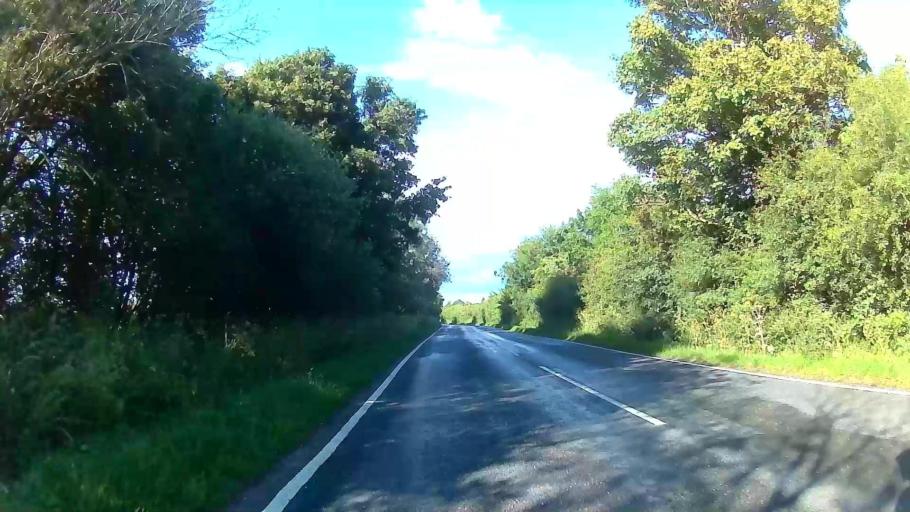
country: GB
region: England
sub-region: Essex
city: Ingatestone
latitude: 51.7041
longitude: 0.3561
